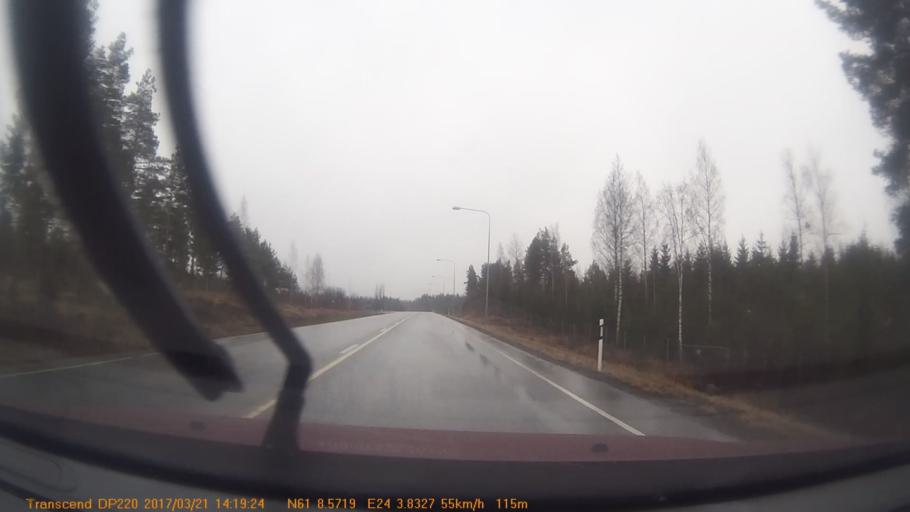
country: FI
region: Haeme
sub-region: Haemeenlinna
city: Kalvola
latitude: 61.1430
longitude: 24.0638
